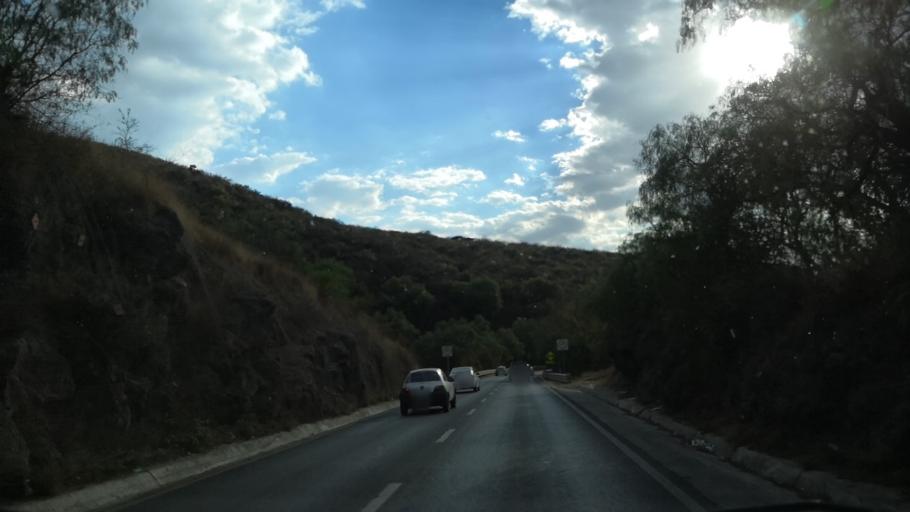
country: MX
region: Guanajuato
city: Marfil
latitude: 21.0043
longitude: -101.2761
